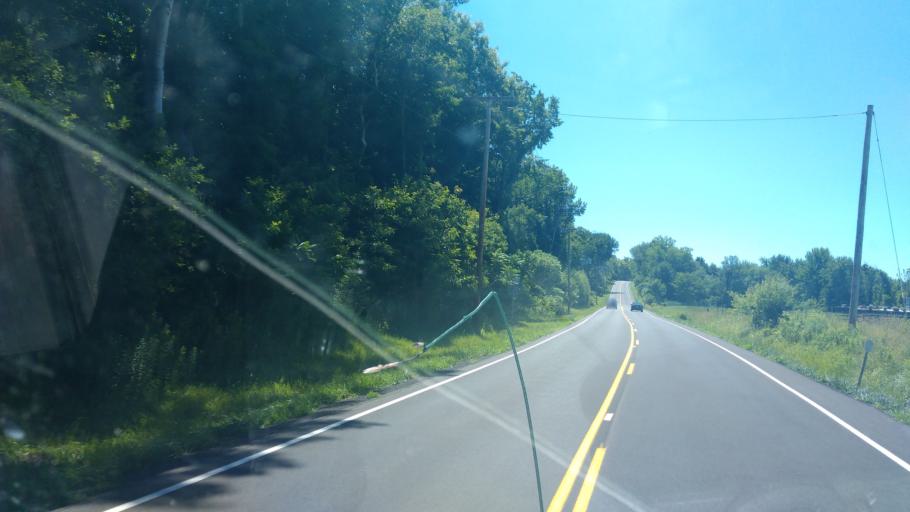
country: US
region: New York
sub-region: Wayne County
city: Sodus
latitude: 43.2425
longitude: -76.9864
